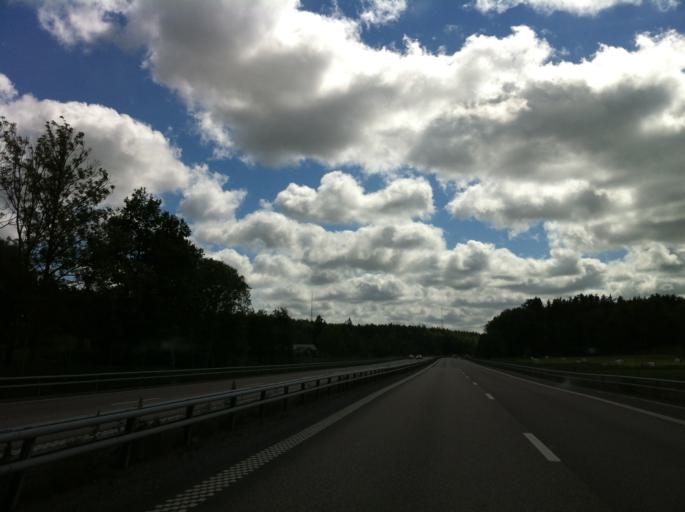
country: SE
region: Vaestra Goetaland
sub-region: Ale Kommun
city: Alvangen
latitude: 57.9505
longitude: 12.1012
